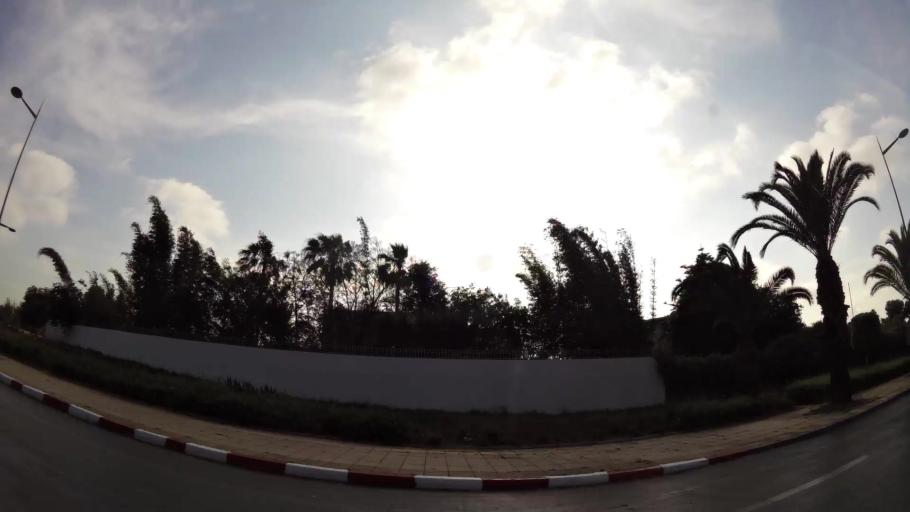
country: MA
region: Rabat-Sale-Zemmour-Zaer
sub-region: Rabat
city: Rabat
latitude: 33.9602
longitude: -6.8263
